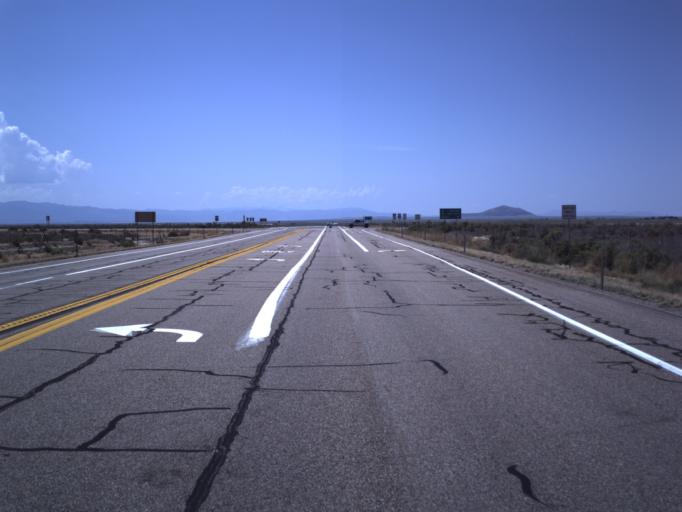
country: US
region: Utah
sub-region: Millard County
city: Delta
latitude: 39.3553
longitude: -112.4966
